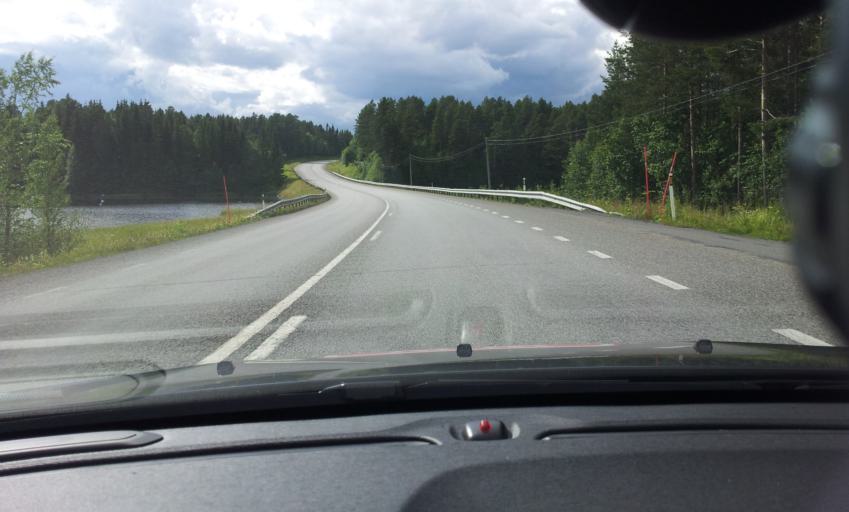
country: SE
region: Jaemtland
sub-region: Are Kommun
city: Jarpen
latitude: 63.3361
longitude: 13.5130
